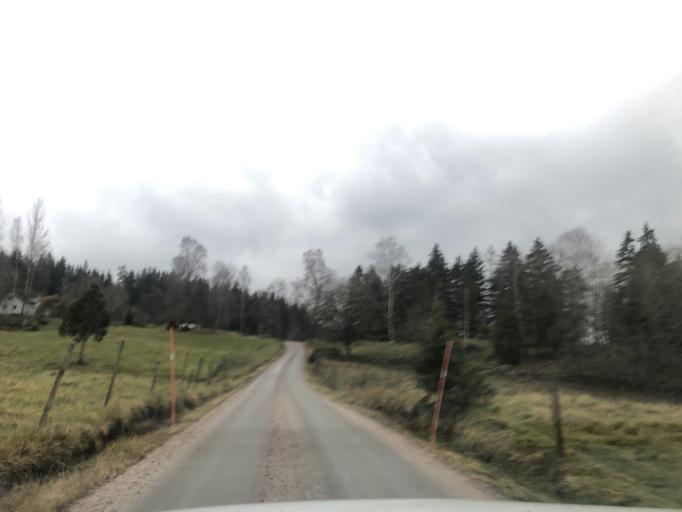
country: SE
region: Vaestra Goetaland
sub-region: Ulricehamns Kommun
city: Ulricehamn
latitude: 57.8964
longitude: 13.4753
